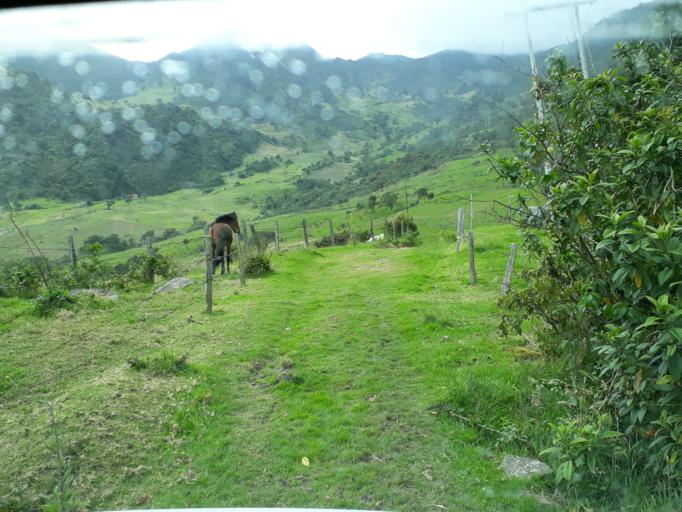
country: CO
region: Cundinamarca
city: Pacho
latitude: 5.1622
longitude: -74.0576
